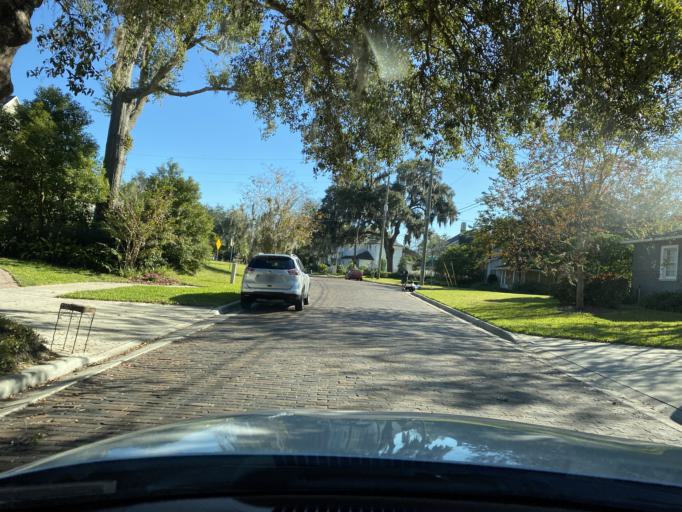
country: US
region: Florida
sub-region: Orange County
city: Orlando
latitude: 28.5626
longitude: -81.3861
